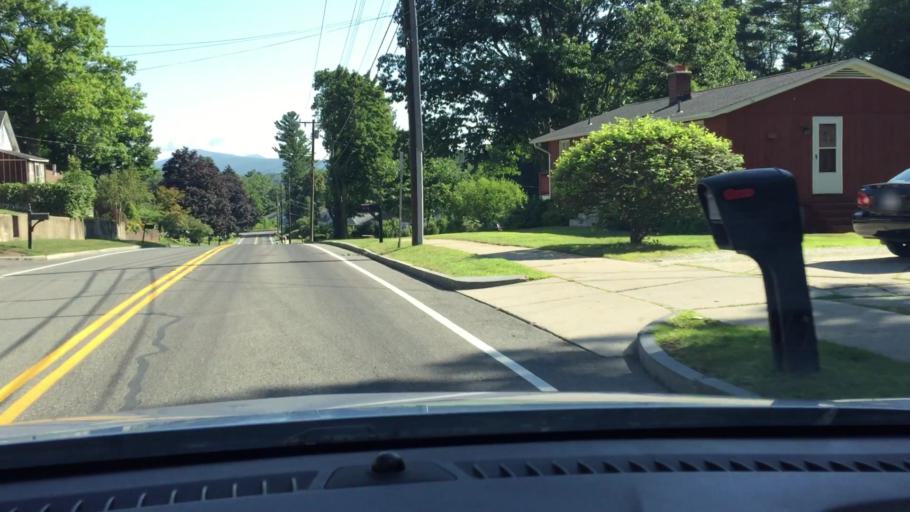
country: US
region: Massachusetts
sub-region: Berkshire County
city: Pittsfield
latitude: 42.4850
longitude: -73.2601
